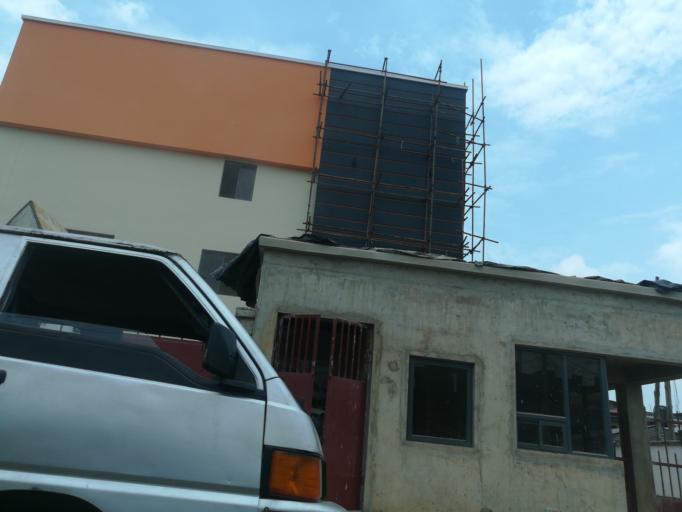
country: NG
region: Lagos
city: Ikeja
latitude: 6.5927
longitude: 3.3596
